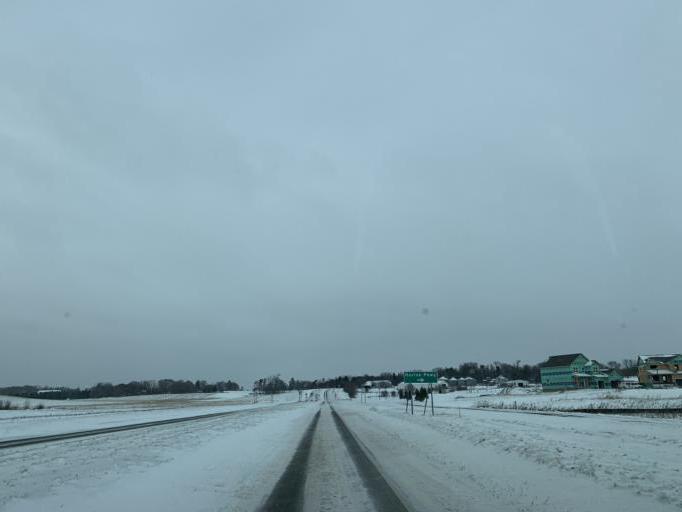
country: US
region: Minnesota
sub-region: Washington County
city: Cottage Grove
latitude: 44.8555
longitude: -92.9236
